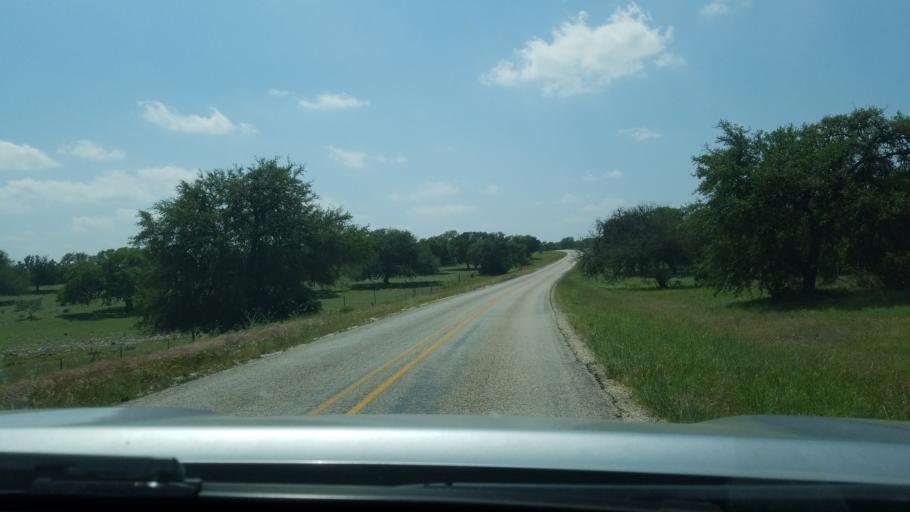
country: US
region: Texas
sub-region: Blanco County
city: Blanco
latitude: 29.9530
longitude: -98.5533
